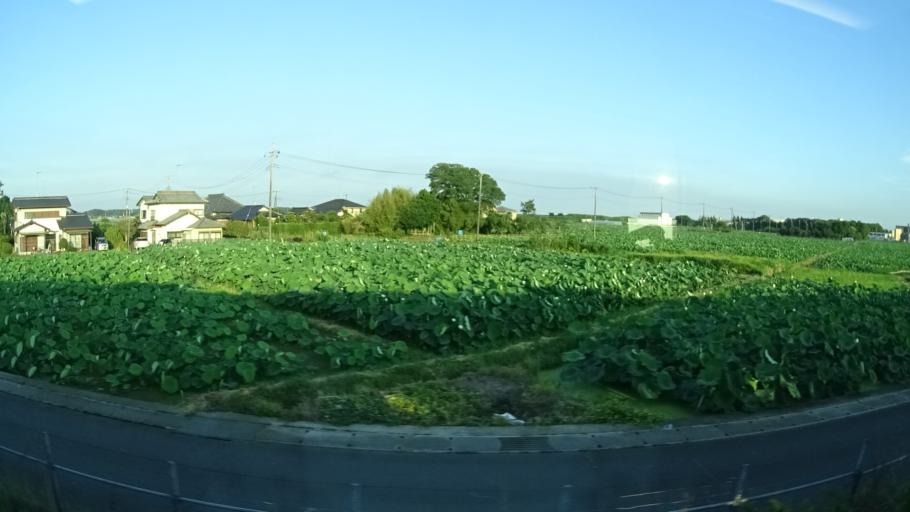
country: JP
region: Ibaraki
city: Ami
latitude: 36.0933
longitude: 140.2148
